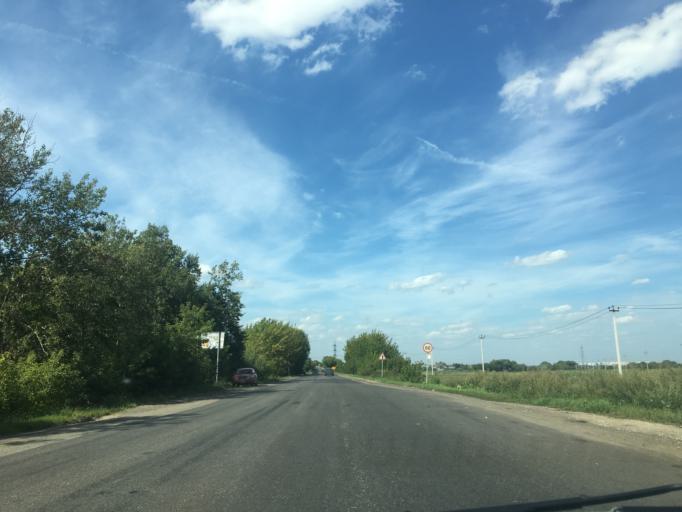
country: RU
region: Moskovskaya
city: Yam
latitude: 55.4549
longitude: 37.6759
